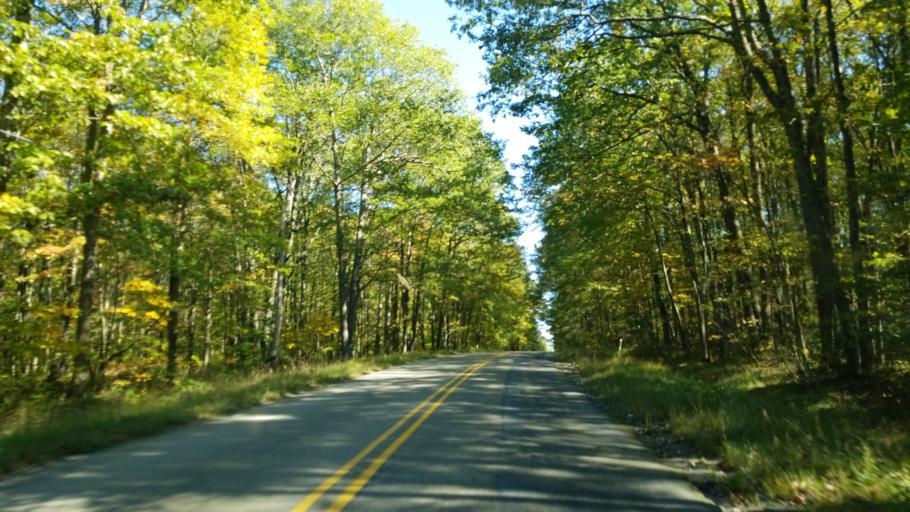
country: US
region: Pennsylvania
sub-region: Clearfield County
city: Shiloh
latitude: 41.2538
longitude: -78.3560
